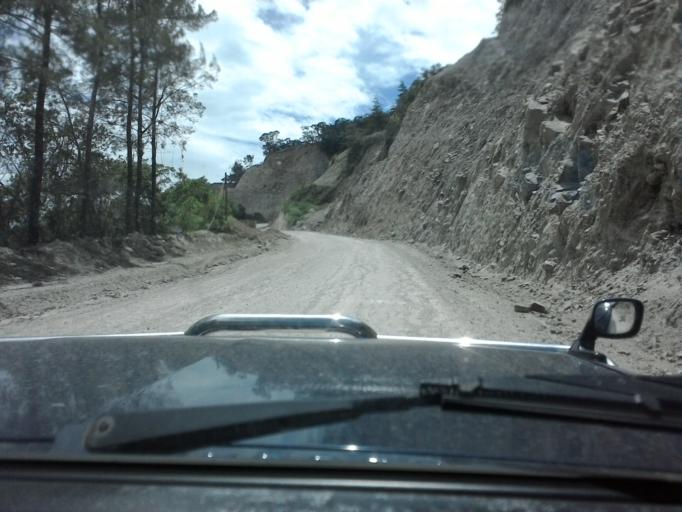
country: CR
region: Guanacaste
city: Juntas
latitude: 10.2968
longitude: -84.8344
